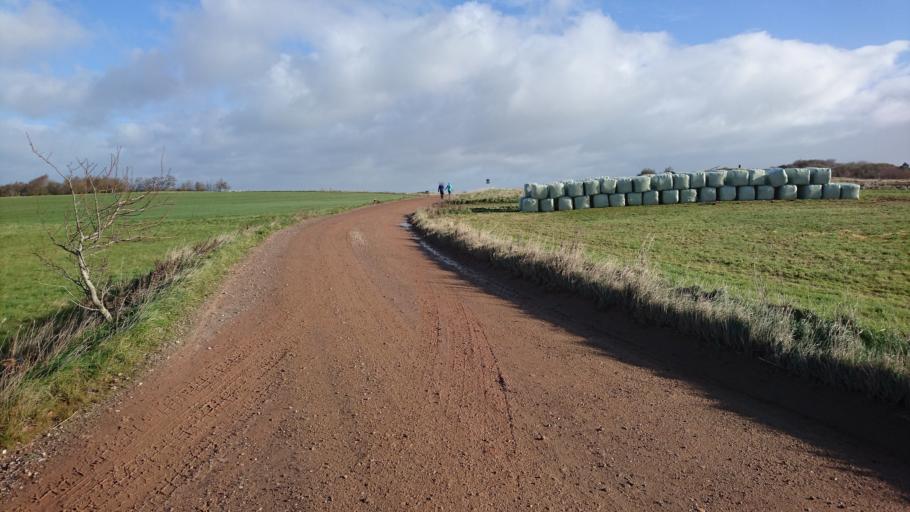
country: DK
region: North Denmark
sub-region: Morso Kommune
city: Nykobing Mors
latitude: 56.8330
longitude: 9.0037
